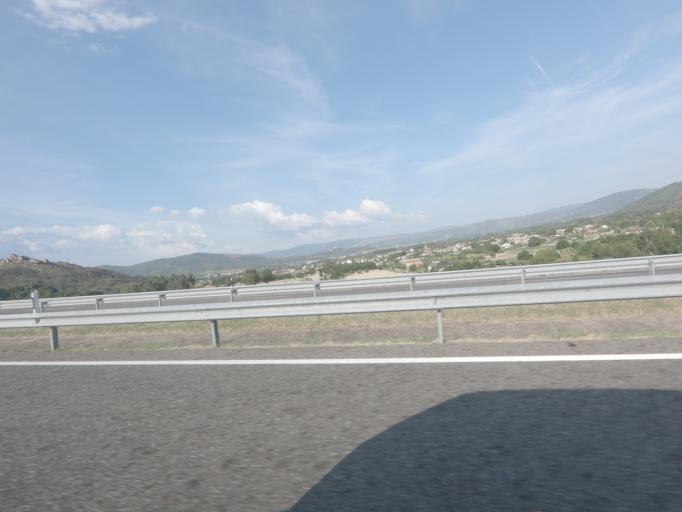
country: ES
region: Galicia
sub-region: Provincia de Ourense
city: Oimbra
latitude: 41.9301
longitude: -7.5007
